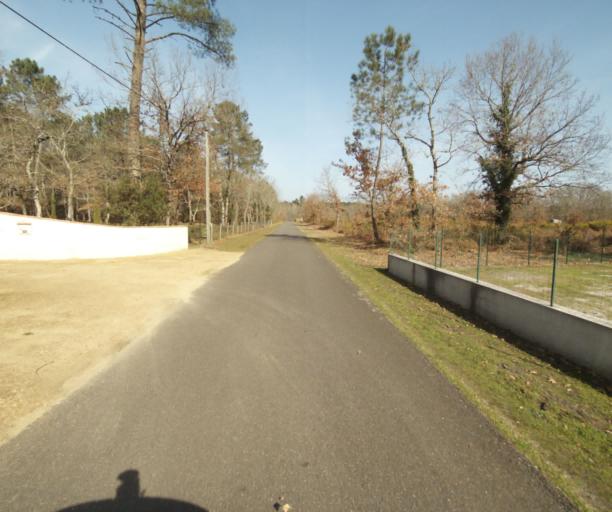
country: FR
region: Aquitaine
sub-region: Departement des Landes
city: Roquefort
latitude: 44.1333
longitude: -0.2490
